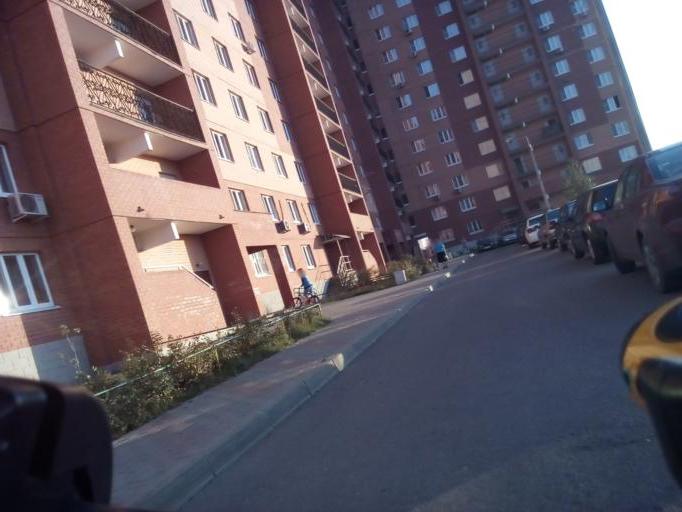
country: RU
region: Moskovskaya
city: Ramenskoye
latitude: 55.5920
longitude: 38.2521
